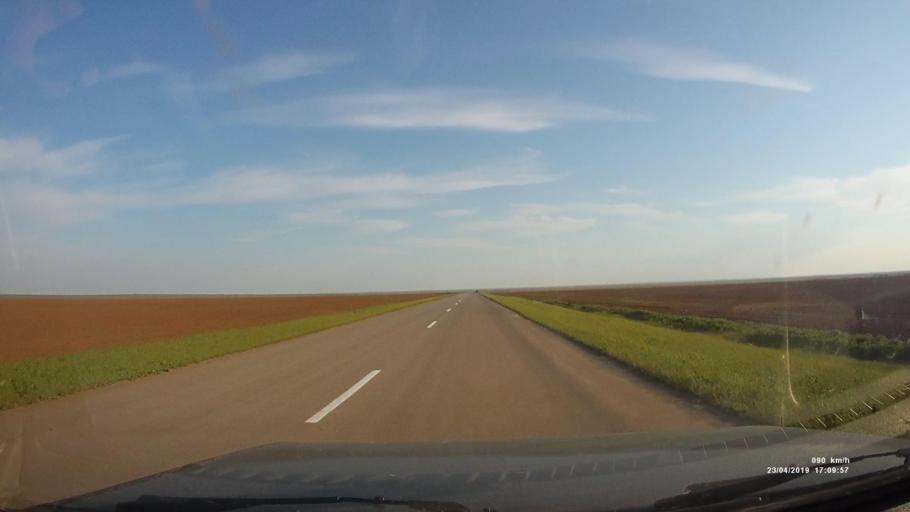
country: RU
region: Kalmykiya
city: Priyutnoye
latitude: 46.2511
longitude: 43.4842
